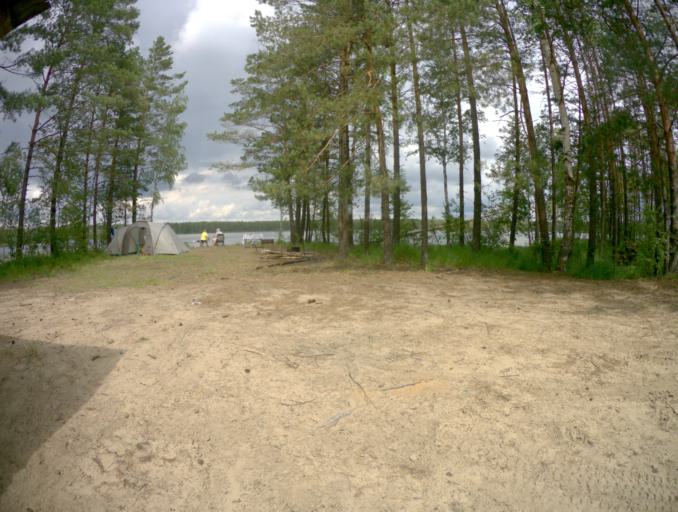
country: RU
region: Nizjnij Novgorod
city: Frolishchi
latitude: 56.3184
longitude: 42.6803
